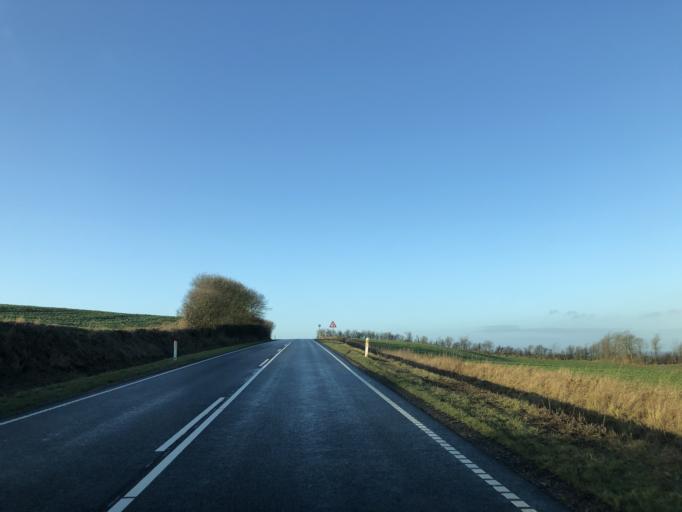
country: DK
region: Central Jutland
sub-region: Lemvig Kommune
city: Lemvig
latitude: 56.5595
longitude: 8.4283
